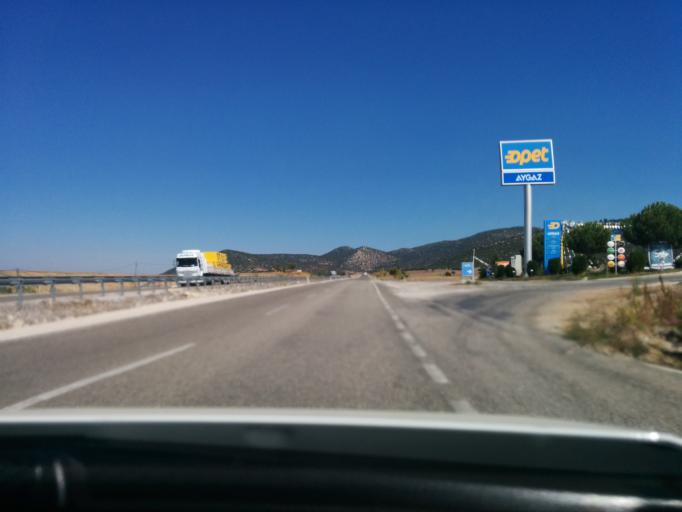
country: TR
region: Antalya
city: Korkuteli
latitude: 37.0081
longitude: 30.3067
